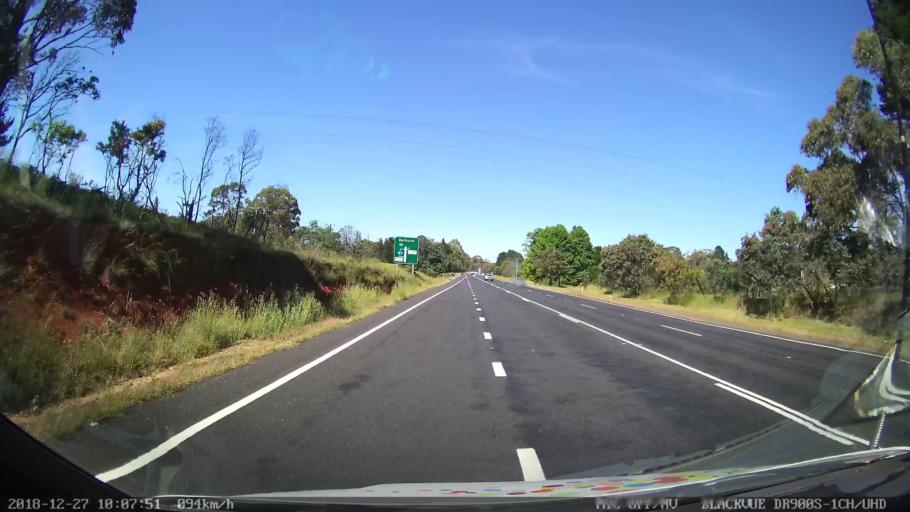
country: AU
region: New South Wales
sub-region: Lithgow
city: Portland
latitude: -33.4433
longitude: 149.8342
